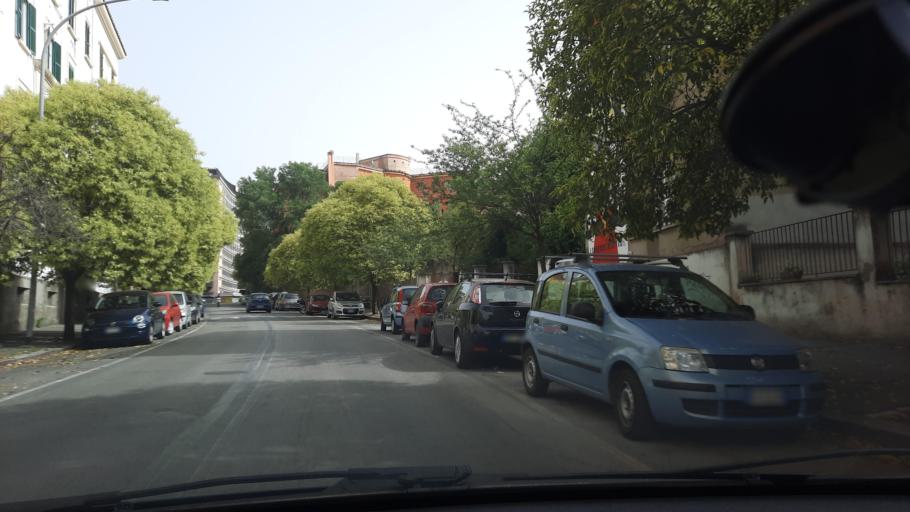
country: IT
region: Latium
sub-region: Citta metropolitana di Roma Capitale
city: Rome
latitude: 41.8613
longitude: 12.4935
